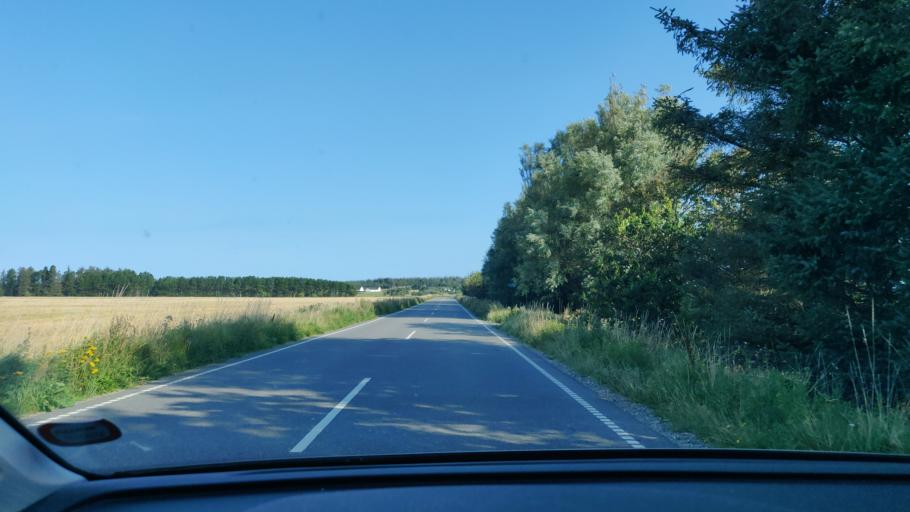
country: DK
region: North Denmark
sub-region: Jammerbugt Kommune
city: Pandrup
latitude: 57.2389
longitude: 9.6498
